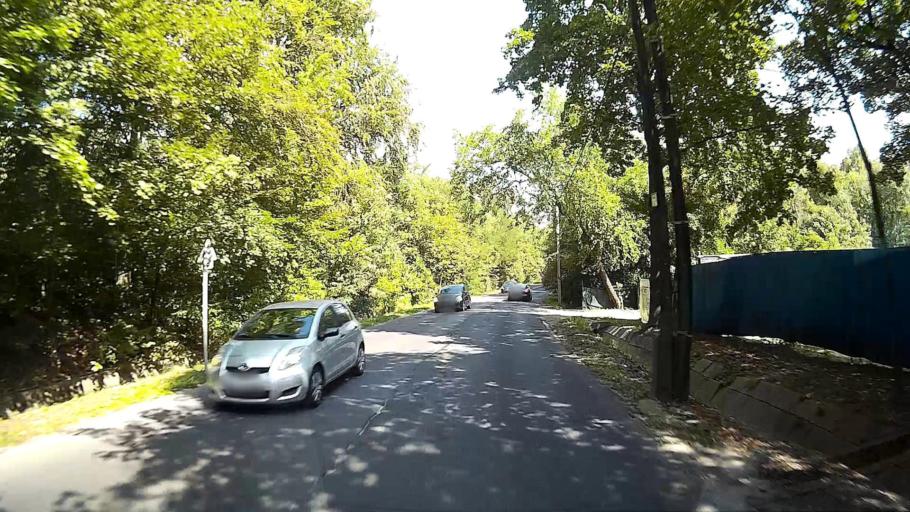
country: HU
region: Pest
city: Budakeszi
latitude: 47.5435
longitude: 18.9513
